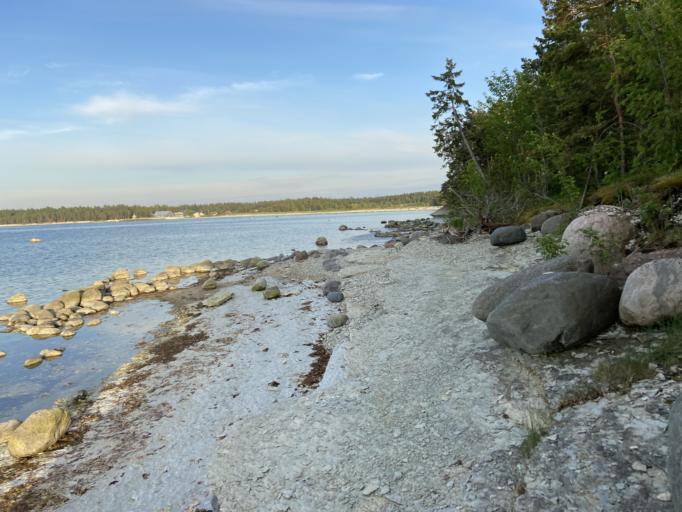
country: EE
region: Harju
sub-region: Paldiski linn
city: Paldiski
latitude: 59.2733
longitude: 23.7335
